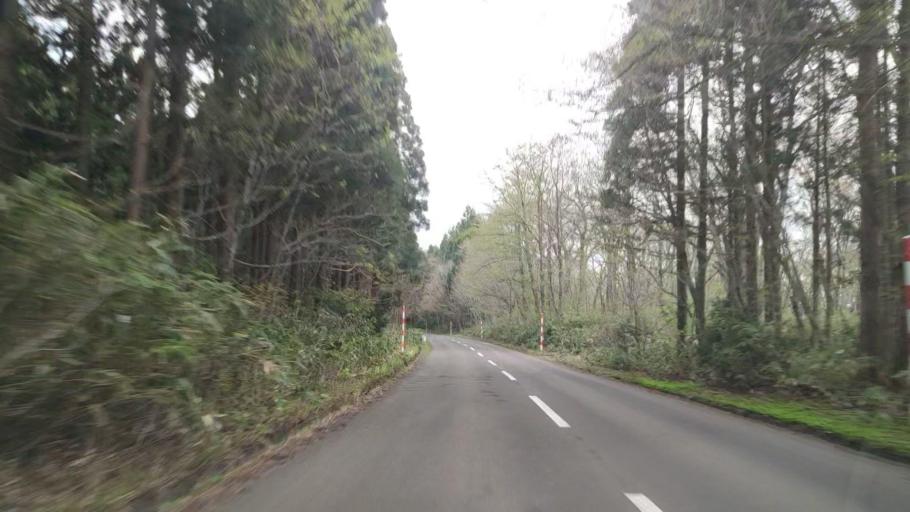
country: JP
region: Akita
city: Hanawa
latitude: 40.3938
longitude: 140.7956
